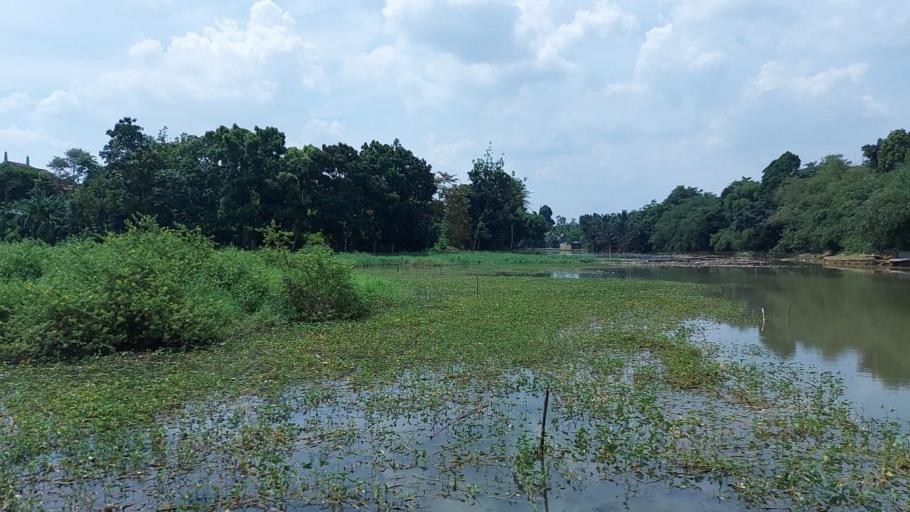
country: ID
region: West Java
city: Cibinong
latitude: -6.4685
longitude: 106.8089
